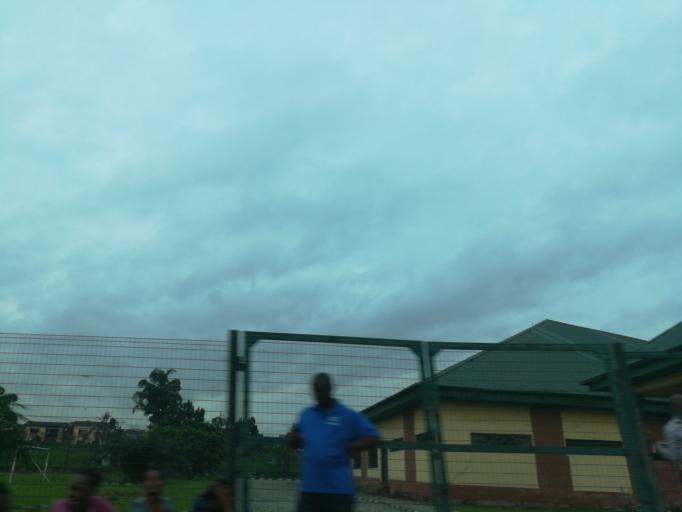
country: NG
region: Rivers
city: Port Harcourt
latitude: 4.8235
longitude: 7.0236
